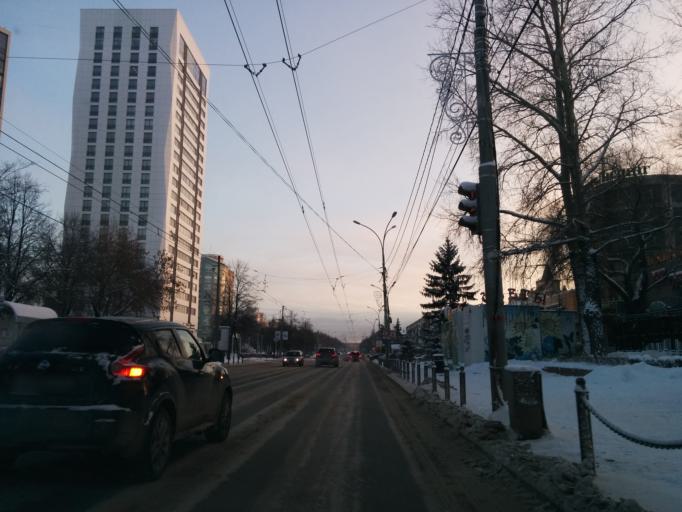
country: RU
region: Perm
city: Perm
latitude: 58.0066
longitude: 56.2530
